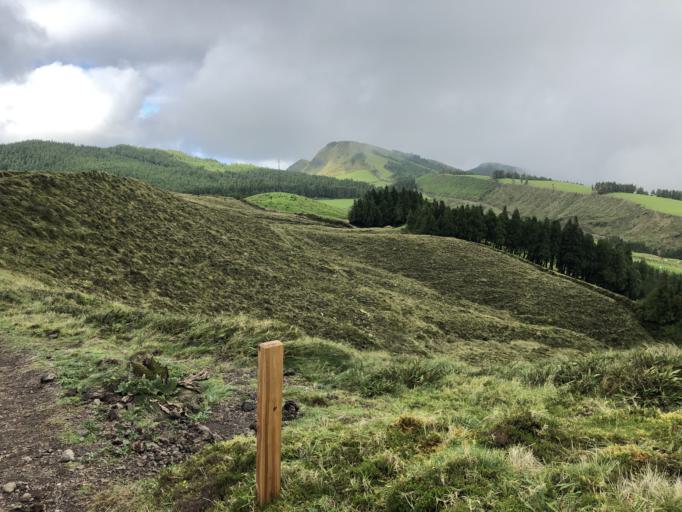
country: PT
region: Azores
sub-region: Ponta Delgada
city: Arrifes
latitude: 37.8314
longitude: -25.7556
